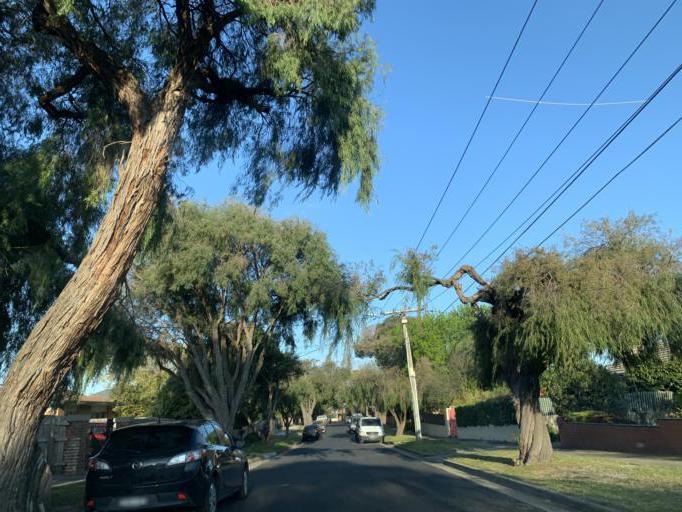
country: AU
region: Victoria
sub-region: Kingston
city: Parkdale
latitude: -37.9843
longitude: 145.0807
